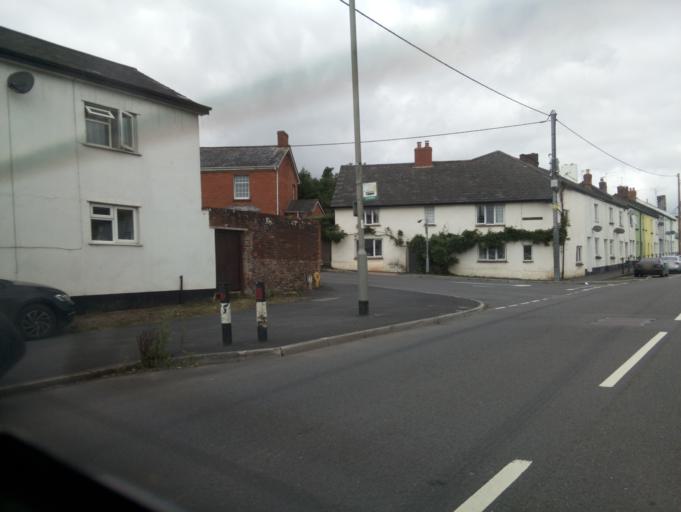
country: GB
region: England
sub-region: Devon
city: Cullompton
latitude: 50.8520
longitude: -3.3944
